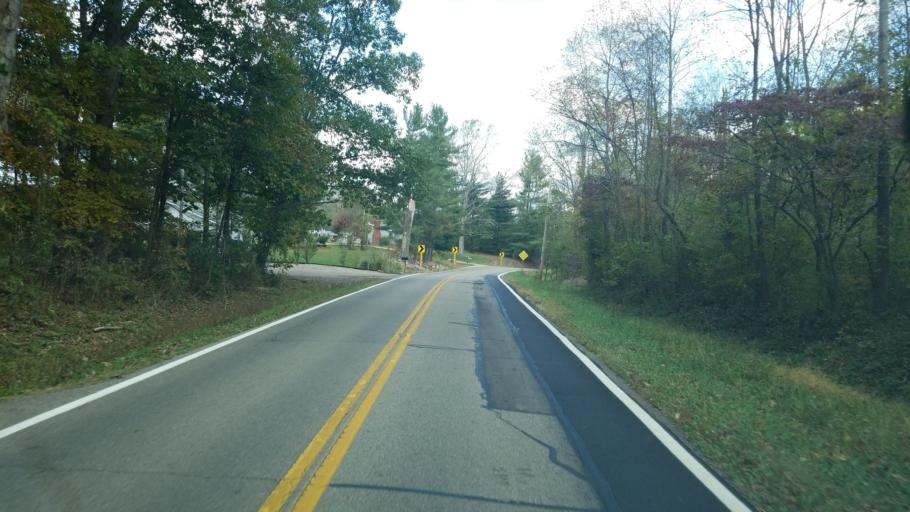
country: US
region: Ohio
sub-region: Jackson County
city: Wellston
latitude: 39.0946
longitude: -82.5812
